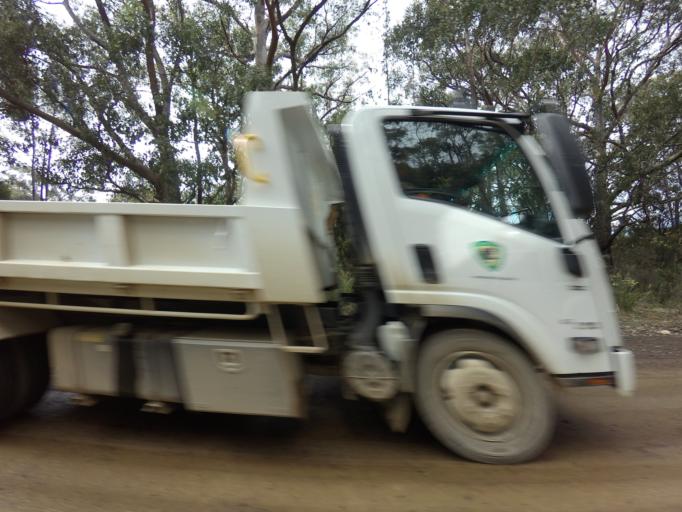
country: AU
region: Tasmania
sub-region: Huon Valley
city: Geeveston
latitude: -43.4470
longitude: 146.9051
